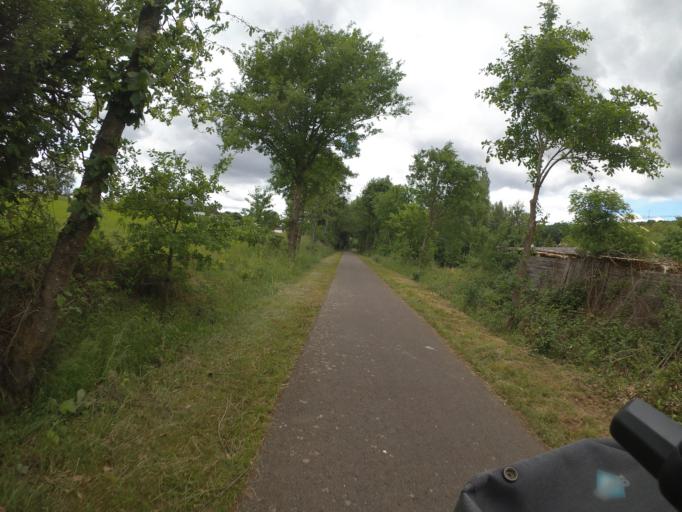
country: DE
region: Rheinland-Pfalz
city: Reichenbach-Steegen
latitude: 49.4970
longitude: 7.5480
